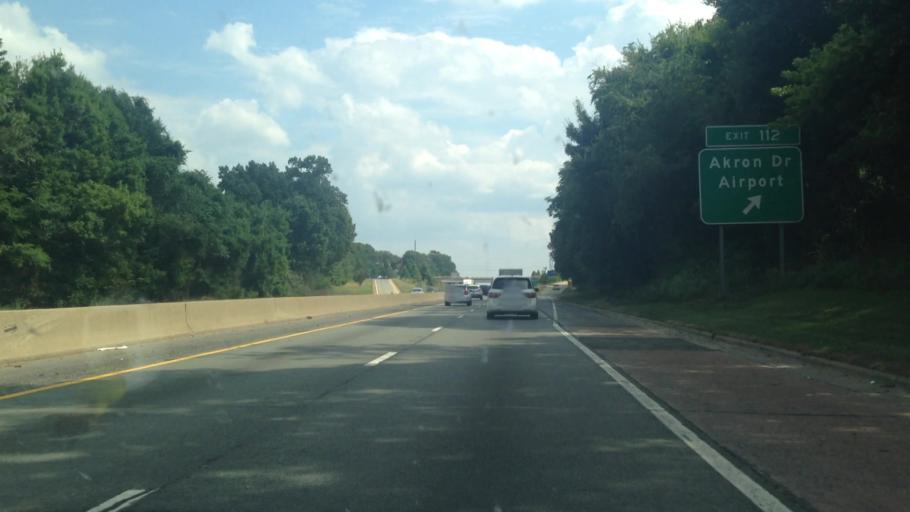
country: US
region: North Carolina
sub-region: Forsyth County
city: Winston-Salem
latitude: 36.1420
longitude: -80.2395
